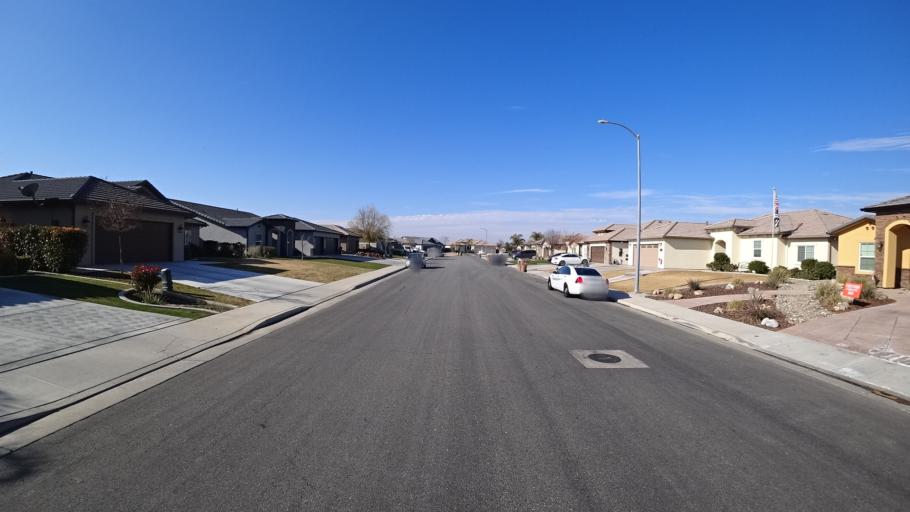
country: US
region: California
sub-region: Kern County
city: Oildale
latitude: 35.4132
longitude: -118.8900
